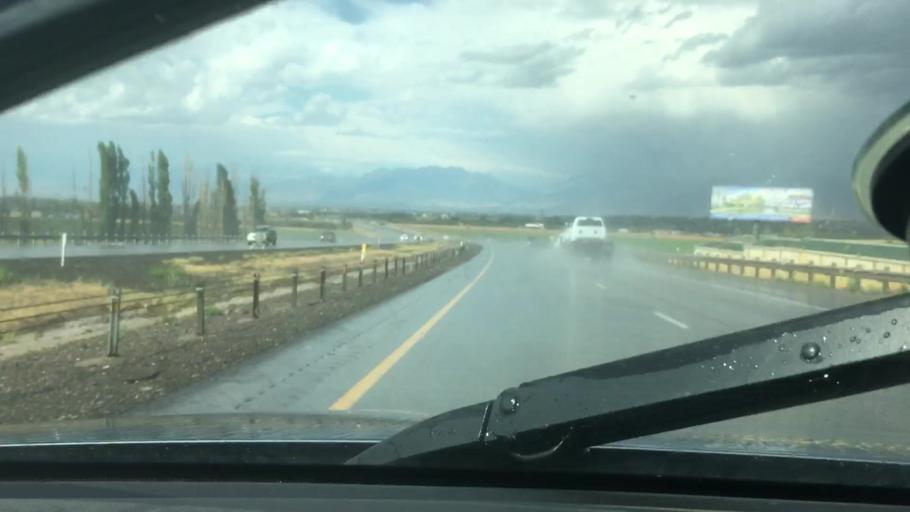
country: US
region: Utah
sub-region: Utah County
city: Santaquin
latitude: 39.9852
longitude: -111.7656
